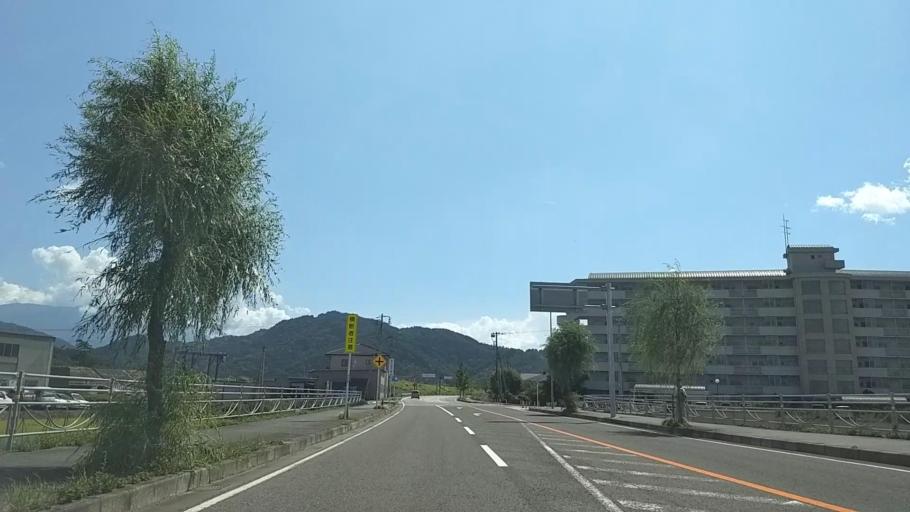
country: JP
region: Yamanashi
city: Ryuo
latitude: 35.5522
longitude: 138.4679
